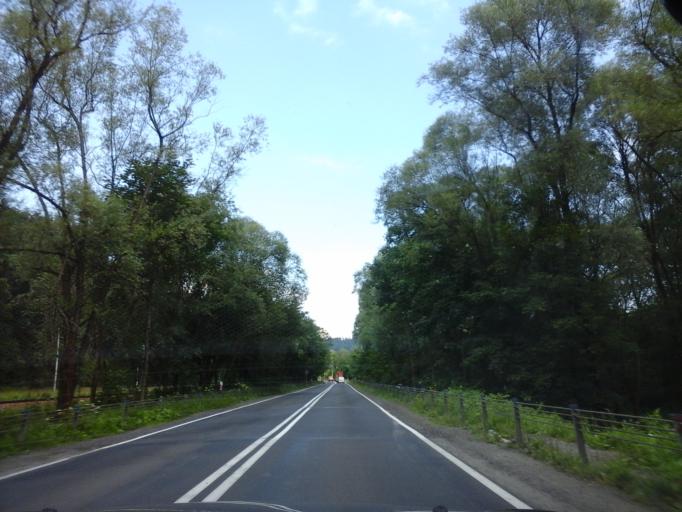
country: PL
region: Lesser Poland Voivodeship
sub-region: Powiat suski
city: Zembrzyce
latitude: 49.7703
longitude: 19.5924
